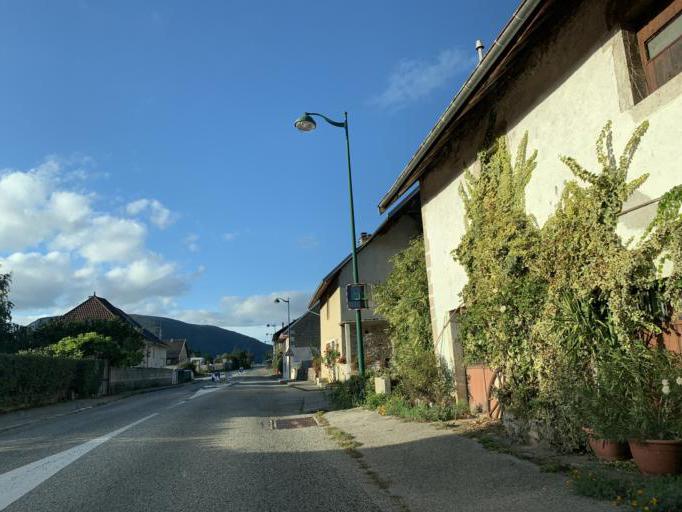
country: FR
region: Rhone-Alpes
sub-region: Departement de l'Ain
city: Virieu-le-Grand
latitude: 45.8234
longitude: 5.6742
